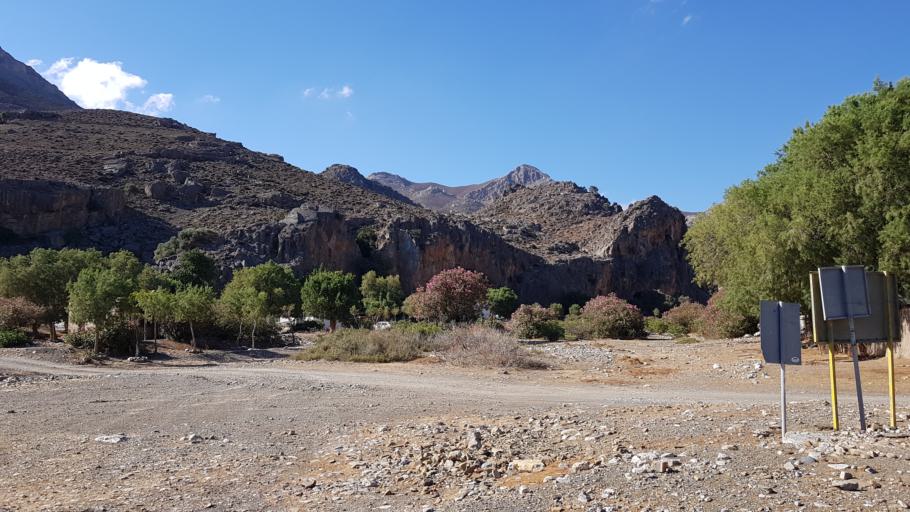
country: GR
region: Crete
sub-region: Nomos Irakleiou
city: Agioi Deka
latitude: 34.9349
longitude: 24.9824
